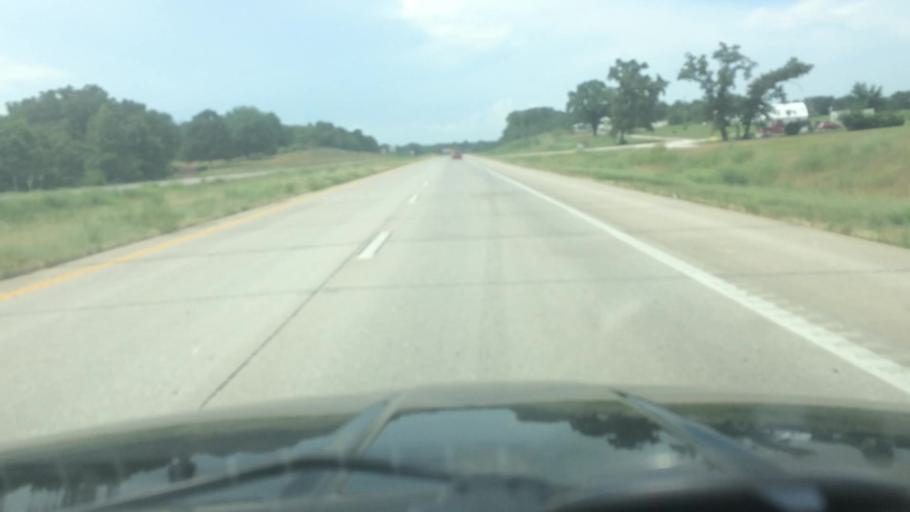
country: US
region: Missouri
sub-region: Saint Clair County
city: Osceola
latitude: 38.0777
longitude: -93.7026
